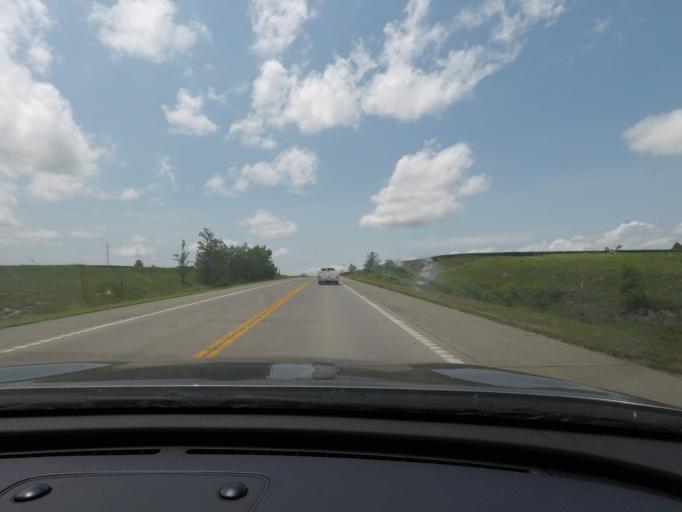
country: US
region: Missouri
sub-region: Carroll County
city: Carrollton
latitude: 39.2031
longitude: -93.4766
